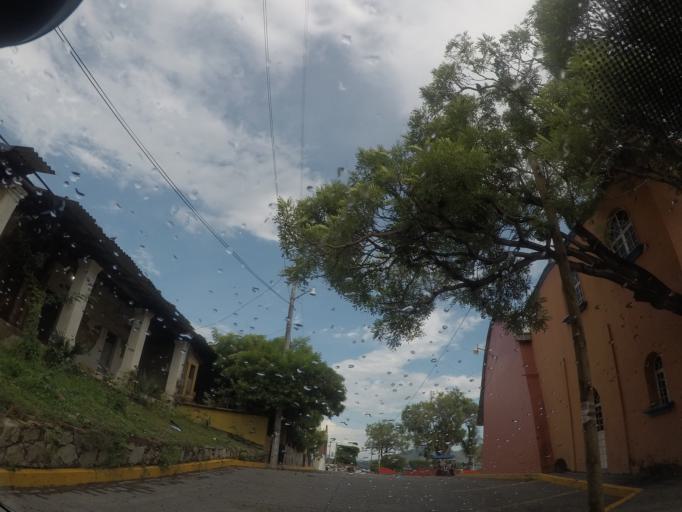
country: MX
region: Oaxaca
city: San Pedro Tapanatepec
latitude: 16.3676
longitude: -94.1945
